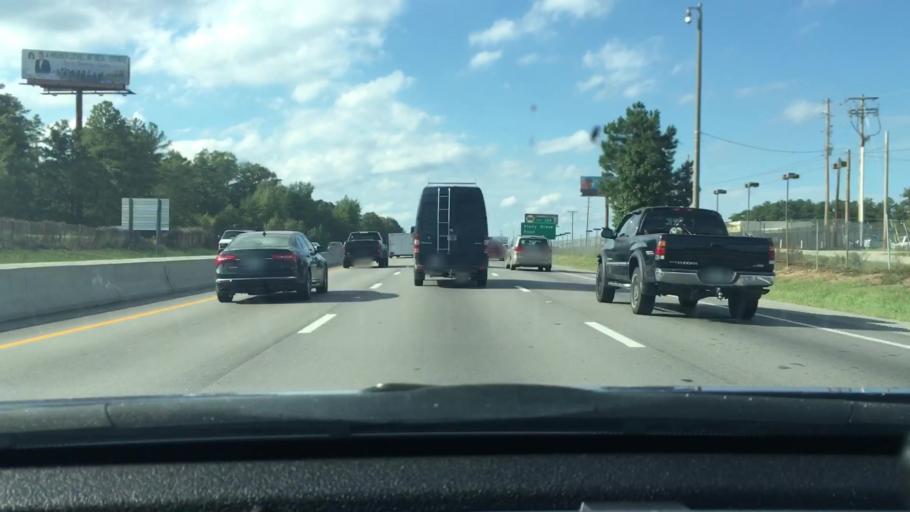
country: US
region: South Carolina
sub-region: Lexington County
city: Saint Andrews
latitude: 34.0532
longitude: -81.1271
